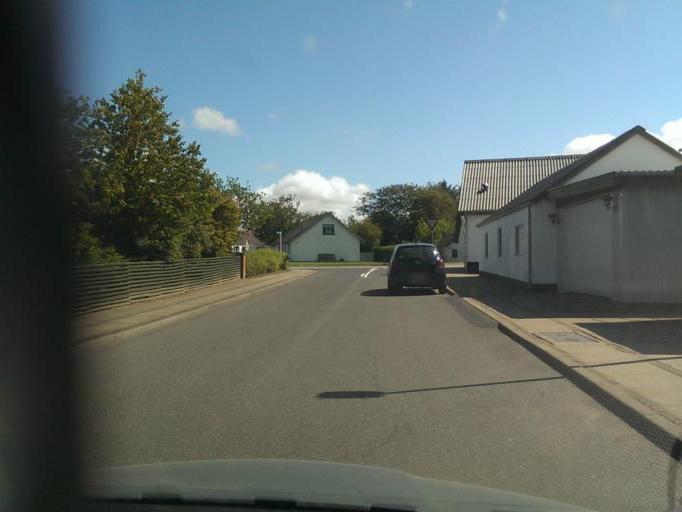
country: DK
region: North Denmark
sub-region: Jammerbugt Kommune
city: Pandrup
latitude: 57.3127
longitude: 9.7071
